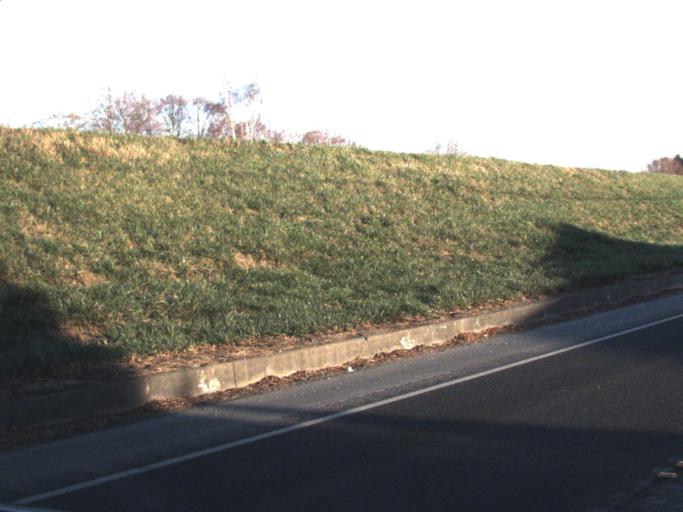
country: US
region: Washington
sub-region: Skagit County
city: Mount Vernon
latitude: 48.4324
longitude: -122.3710
